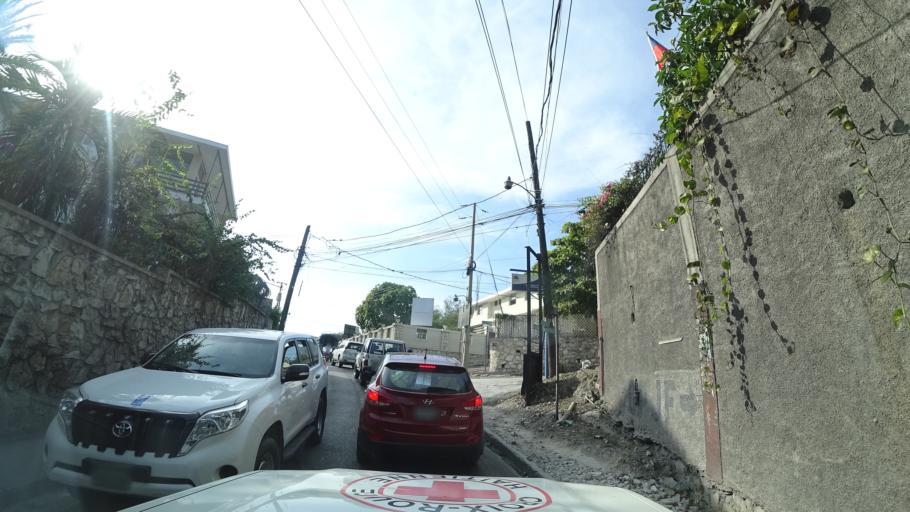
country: HT
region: Ouest
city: Delmas 73
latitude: 18.5307
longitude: -72.2993
